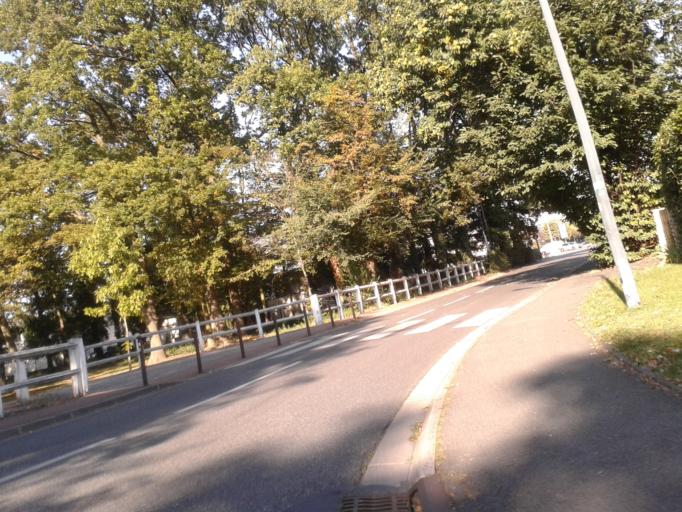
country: FR
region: Ile-de-France
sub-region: Departement du Val-d'Oise
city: Montigny-les-Cormeilles
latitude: 48.9950
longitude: 2.1896
